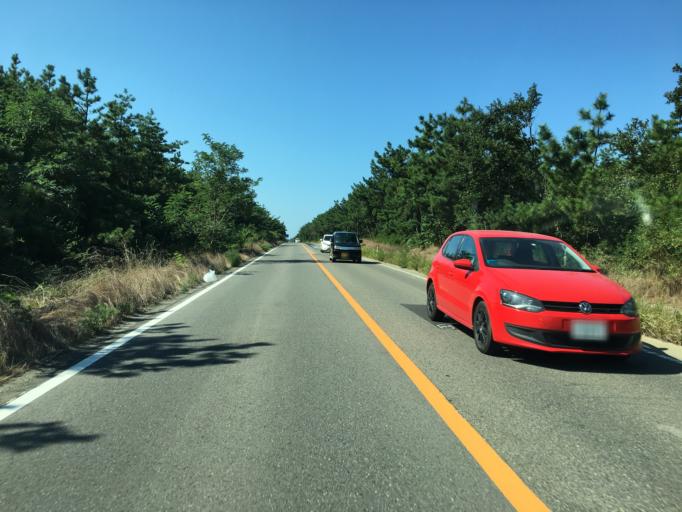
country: JP
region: Niigata
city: Niigata-shi
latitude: 37.9045
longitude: 138.9959
